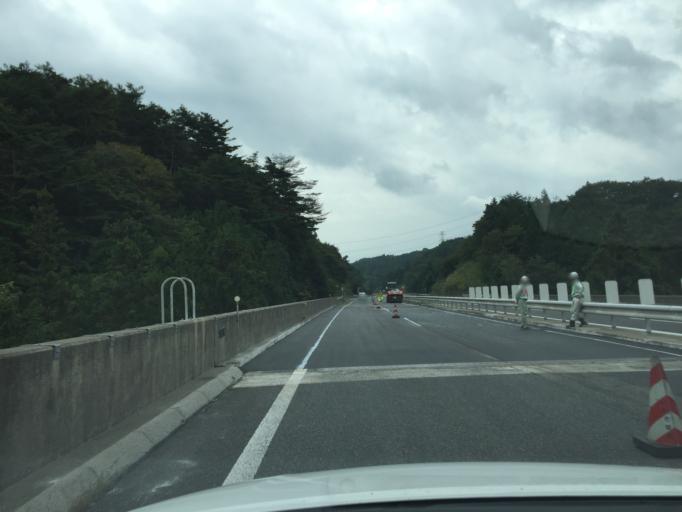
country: JP
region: Fukushima
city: Iwaki
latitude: 37.1729
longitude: 140.7230
